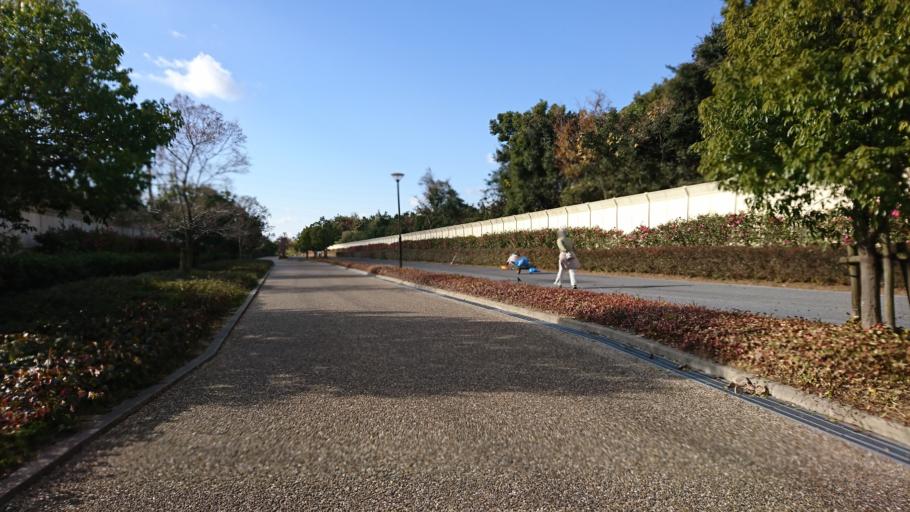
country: JP
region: Hyogo
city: Kakogawacho-honmachi
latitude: 34.7502
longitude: 134.7818
